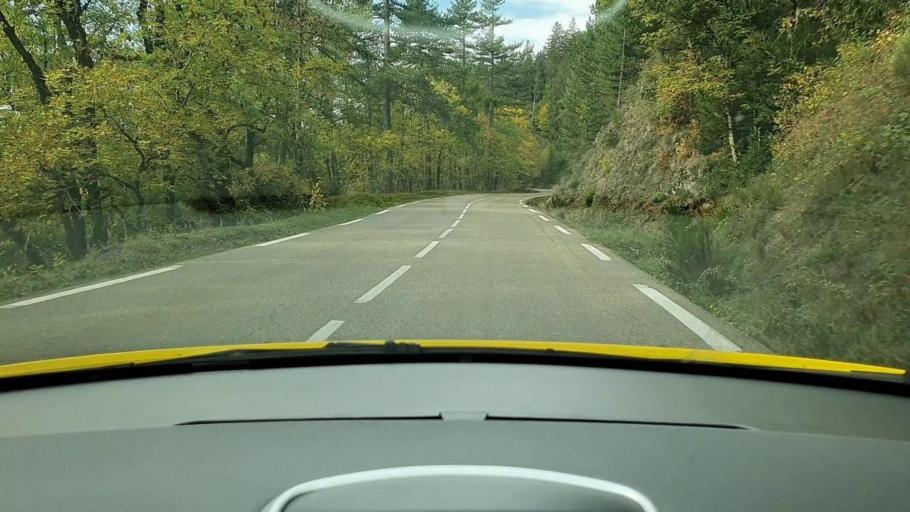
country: FR
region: Languedoc-Roussillon
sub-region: Departement de la Lozere
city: Meyrueis
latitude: 44.1246
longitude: 3.4535
